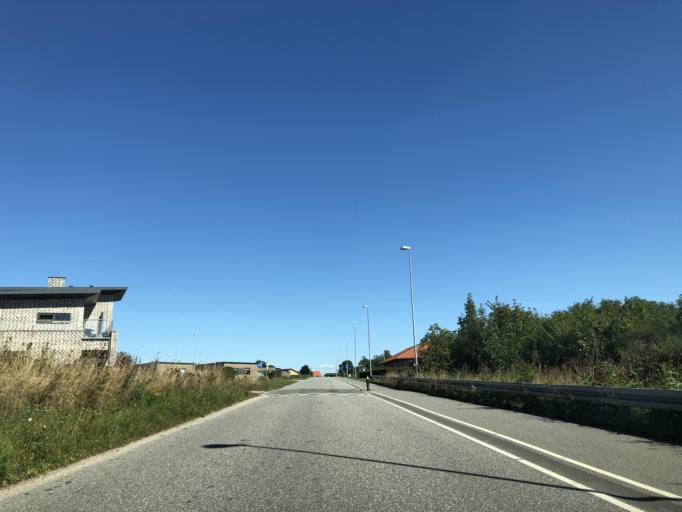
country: DK
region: North Denmark
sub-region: Mariagerfjord Kommune
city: Hobro
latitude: 56.6422
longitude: 9.7767
